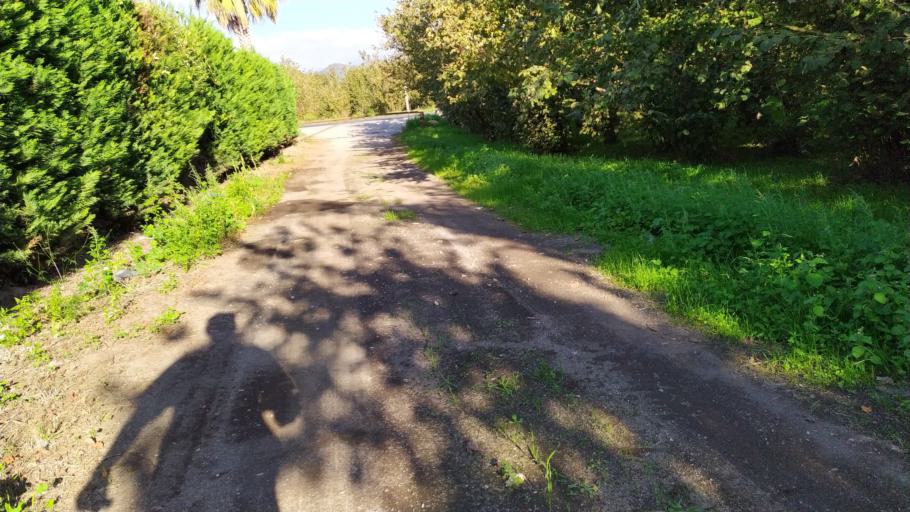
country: IT
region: Campania
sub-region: Provincia di Napoli
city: Piazzolla
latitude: 40.8917
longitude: 14.5312
